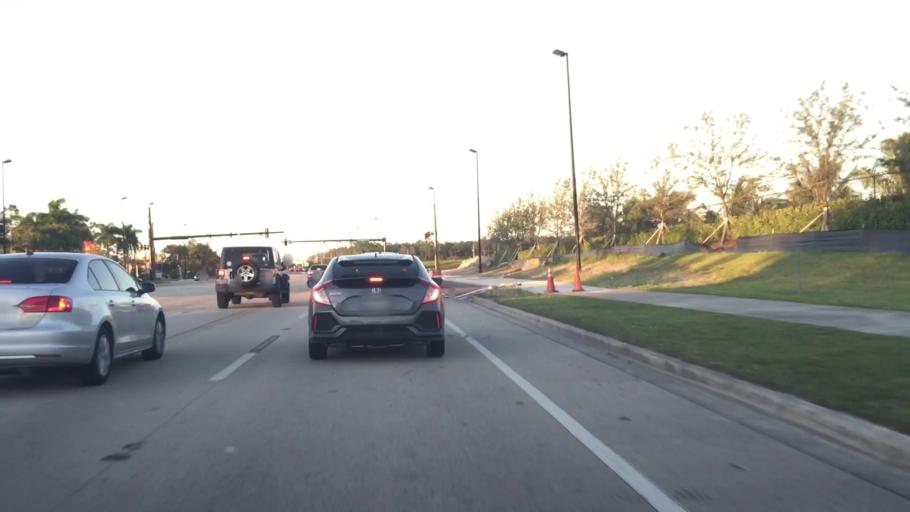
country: US
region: Florida
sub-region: Lee County
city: Three Oaks
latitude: 26.4877
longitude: -81.7838
